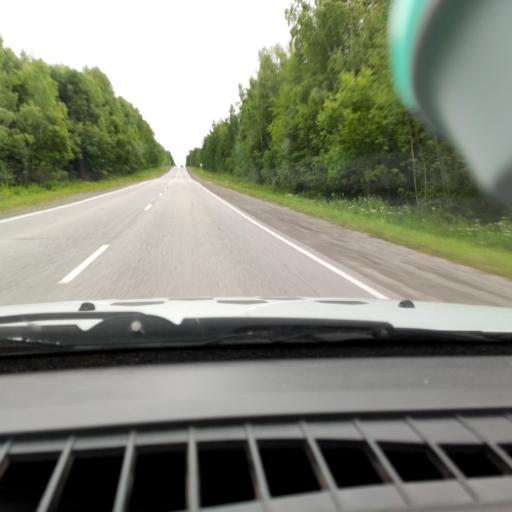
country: RU
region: Perm
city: Lys'va
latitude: 58.1471
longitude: 57.7543
